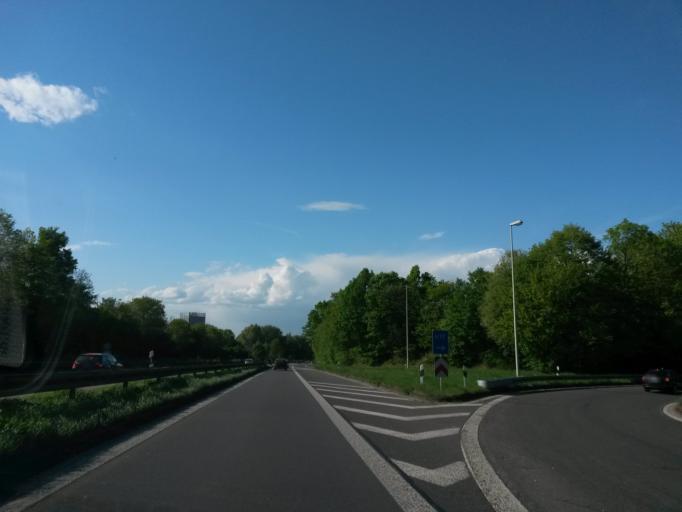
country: DE
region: North Rhine-Westphalia
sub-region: Regierungsbezirk Koln
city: Bonn
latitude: 50.7052
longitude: 7.0632
